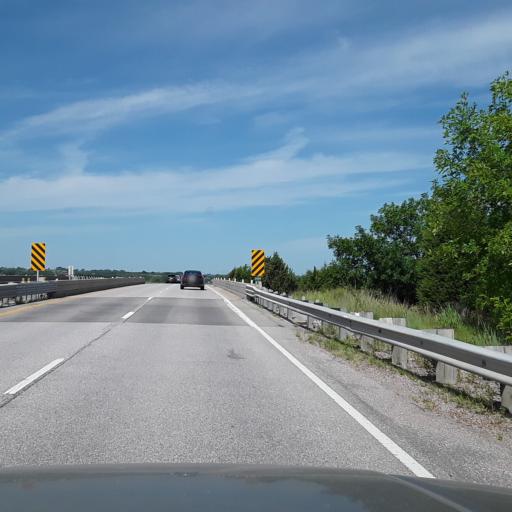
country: US
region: Nebraska
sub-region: Lancaster County
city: Lincoln
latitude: 40.8796
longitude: -96.7581
